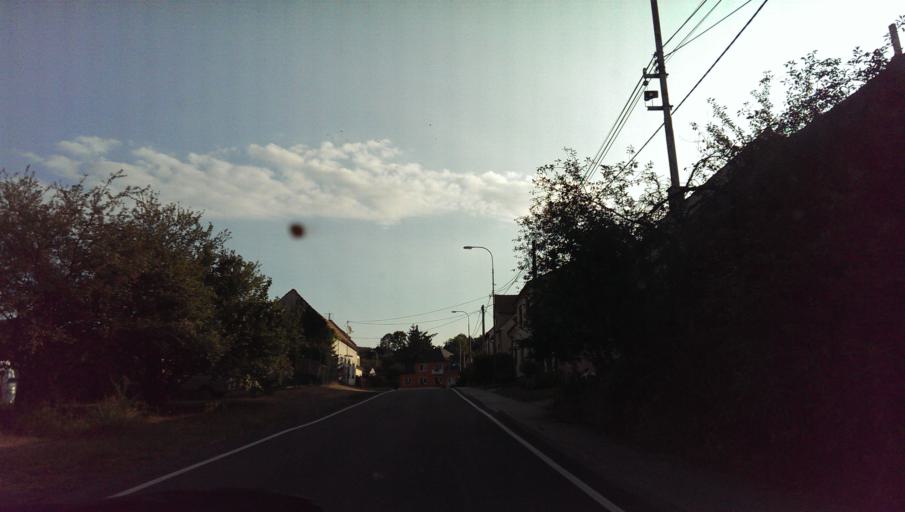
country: CZ
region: South Moravian
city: Zeravice
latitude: 49.0629
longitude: 17.2221
